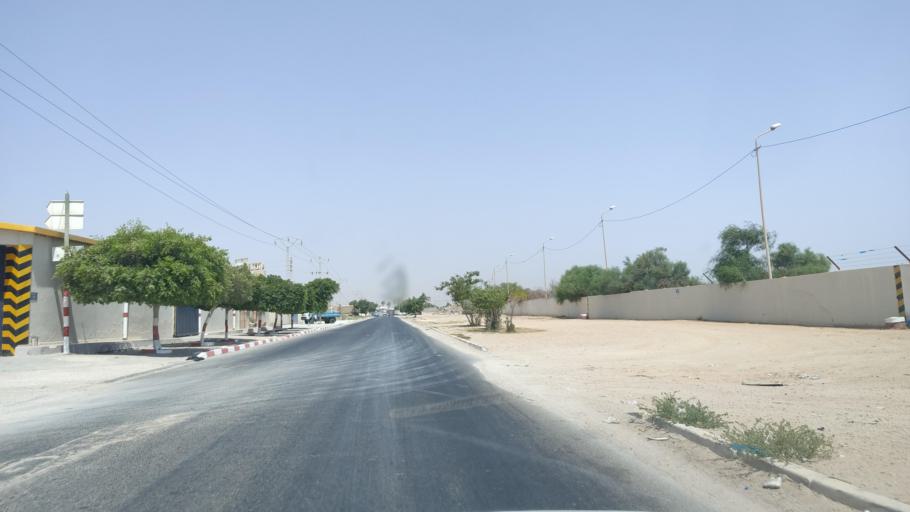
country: TN
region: Safaqis
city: Sfax
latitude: 34.6960
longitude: 10.7225
